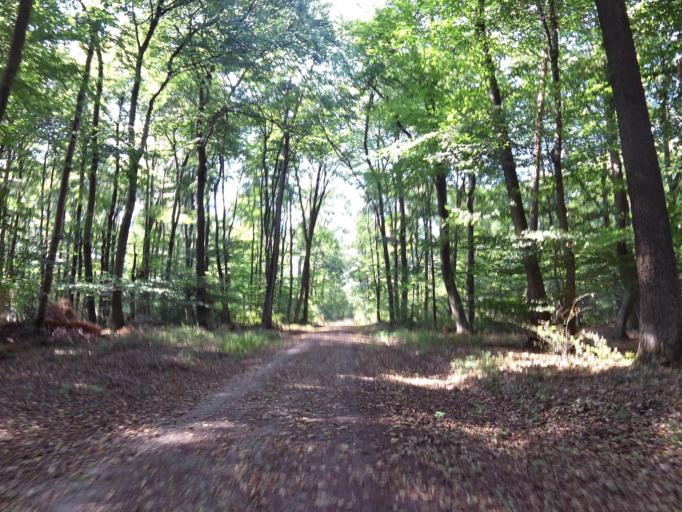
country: DE
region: Hesse
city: Morfelden-Walldorf
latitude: 50.0195
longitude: 8.5699
